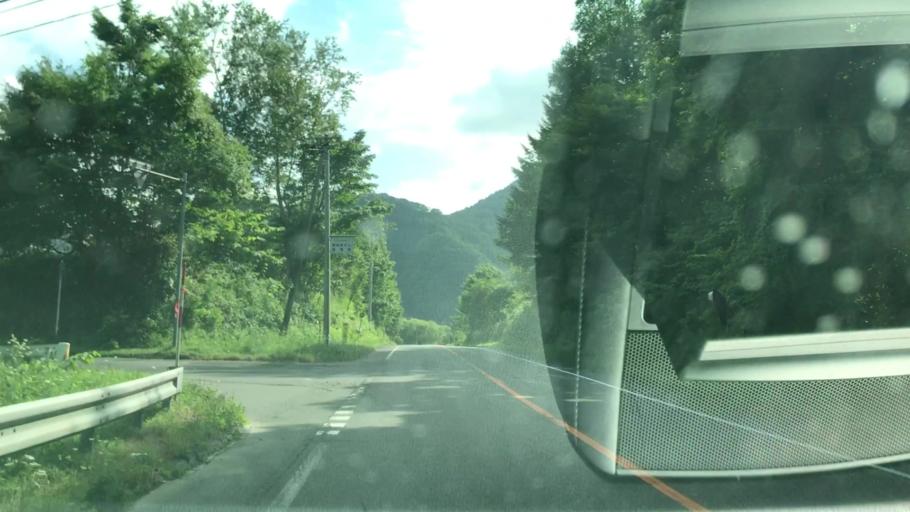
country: JP
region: Hokkaido
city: Shizunai-furukawacho
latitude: 42.7998
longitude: 142.3973
